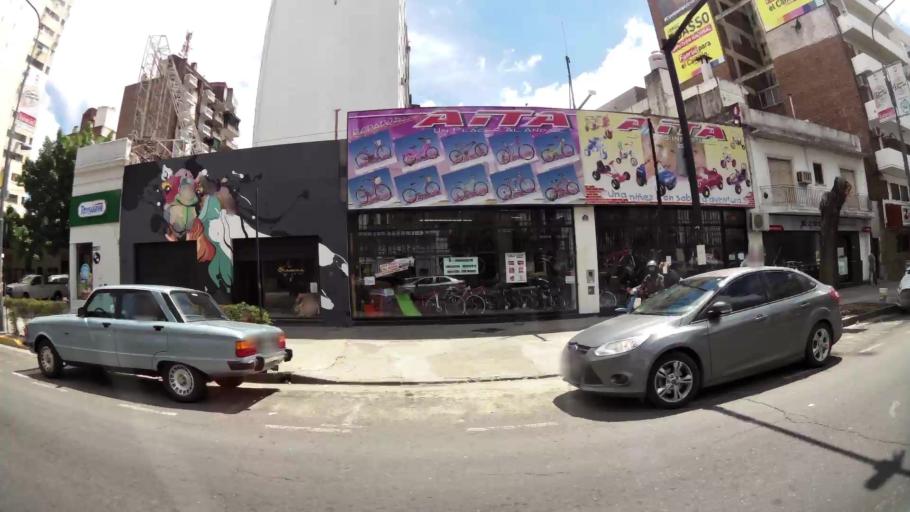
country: AR
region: Santa Fe
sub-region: Departamento de Rosario
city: Rosario
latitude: -32.9559
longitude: -60.6491
